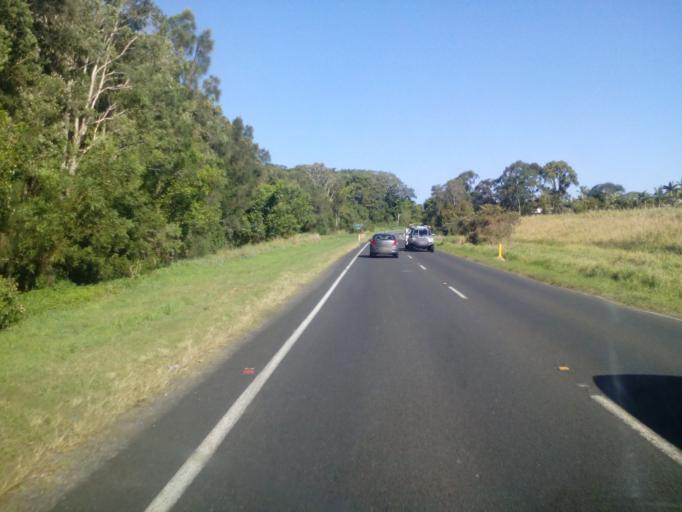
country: AU
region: New South Wales
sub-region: Tweed
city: Kingscliff
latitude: -28.2594
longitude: 153.5607
